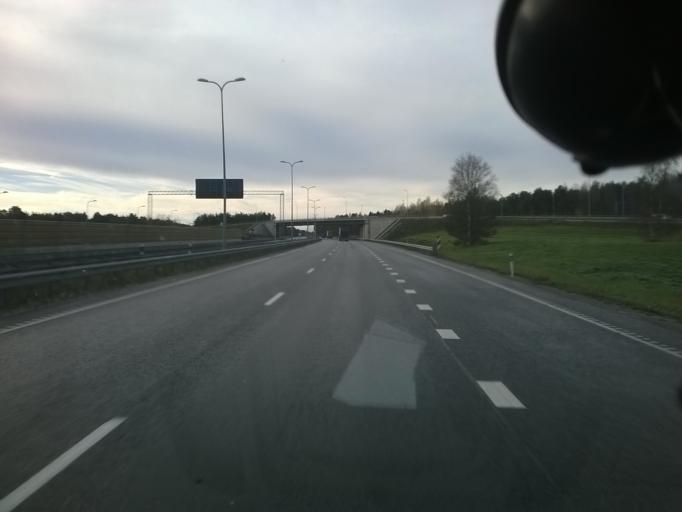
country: EE
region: Harju
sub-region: Kiili vald
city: Kiili
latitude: 59.3232
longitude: 24.7684
